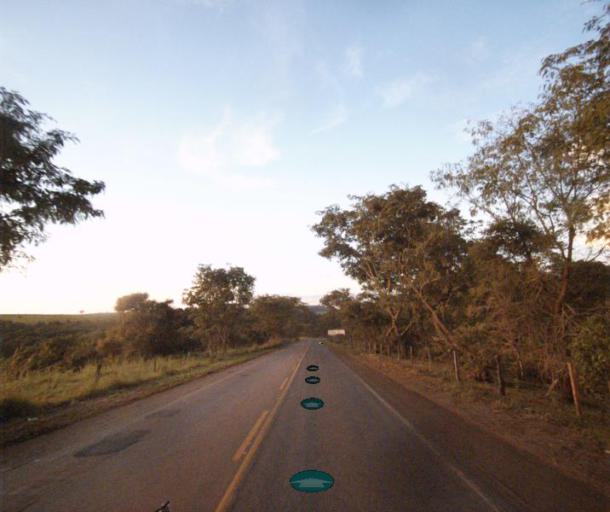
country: BR
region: Goias
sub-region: Pirenopolis
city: Pirenopolis
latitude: -15.9957
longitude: -48.8382
